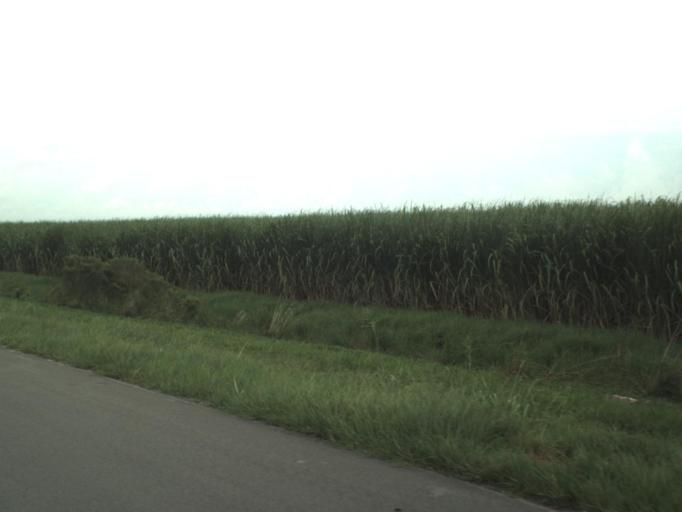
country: US
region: Florida
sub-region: Palm Beach County
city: Belle Glade
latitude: 26.7264
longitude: -80.6224
